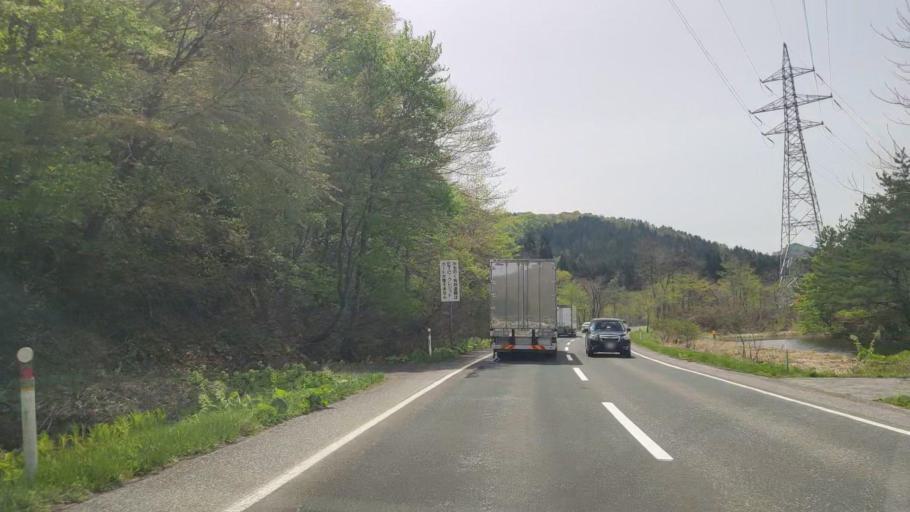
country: JP
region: Aomori
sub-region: Misawa Shi
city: Inuotose
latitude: 40.7883
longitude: 141.0843
